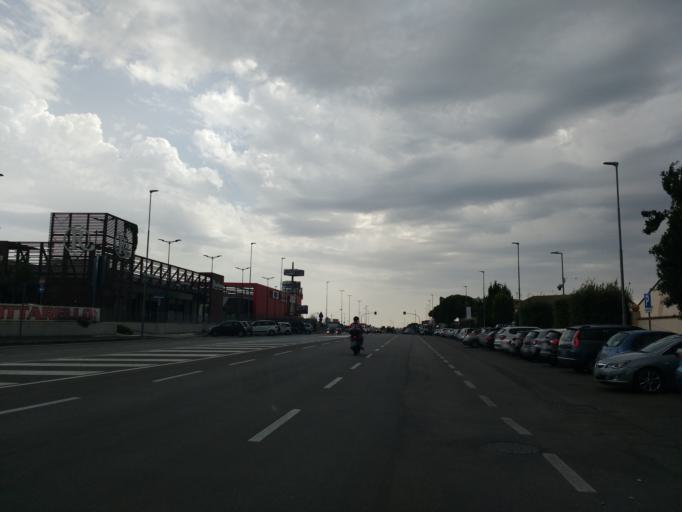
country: IT
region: Latium
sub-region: Citta metropolitana di Roma Capitale
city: Monte Migliore-La Selvotta
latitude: 41.7169
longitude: 12.4461
